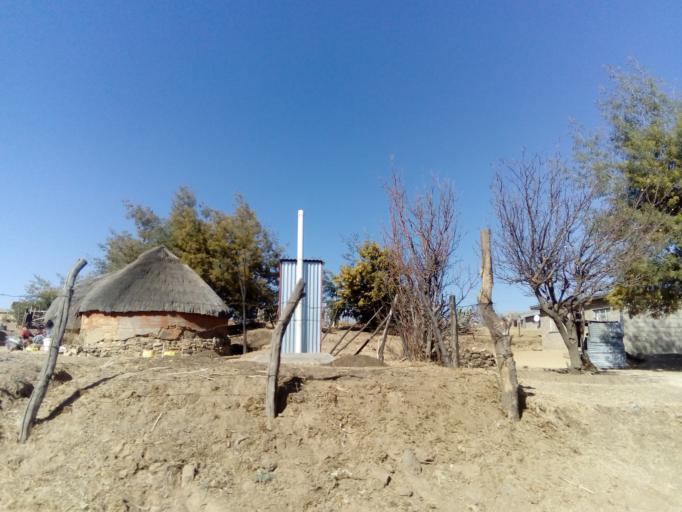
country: LS
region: Berea
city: Teyateyaneng
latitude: -29.1399
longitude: 27.8723
